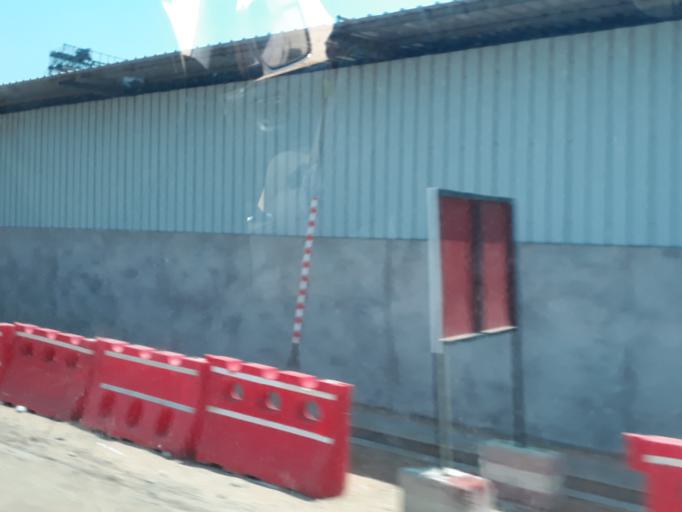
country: LK
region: Western
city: Colombo
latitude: 6.9396
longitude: 79.8360
